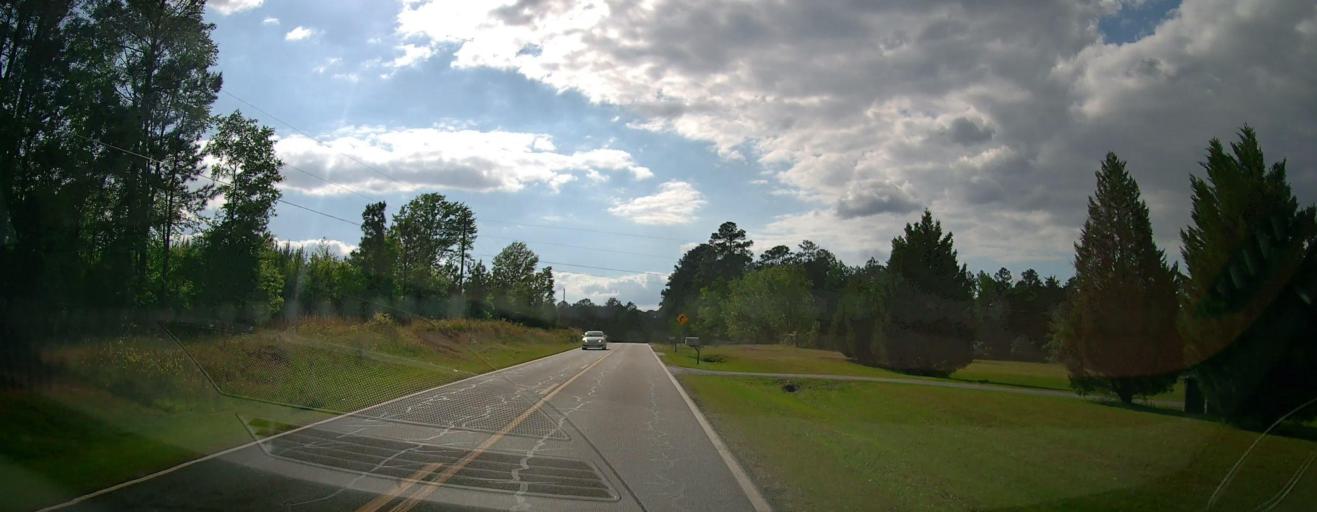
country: US
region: Georgia
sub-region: Baldwin County
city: Hardwick
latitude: 33.0637
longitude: -83.1649
